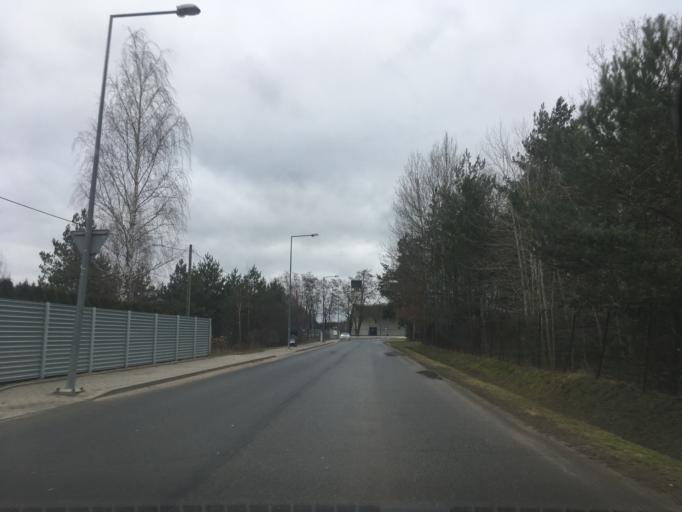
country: PL
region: Masovian Voivodeship
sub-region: Powiat piaseczynski
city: Lesznowola
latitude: 52.0556
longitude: 20.8955
